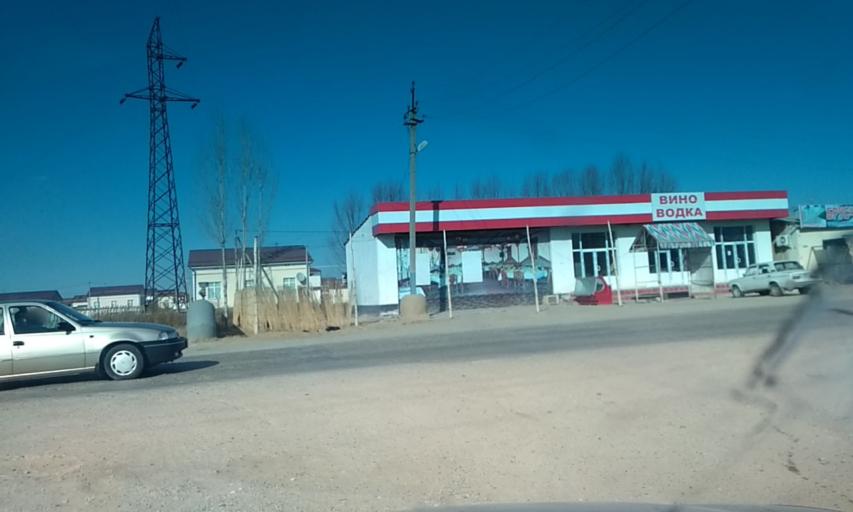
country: UZ
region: Sirdaryo
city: Guliston
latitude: 40.4933
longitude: 68.8128
